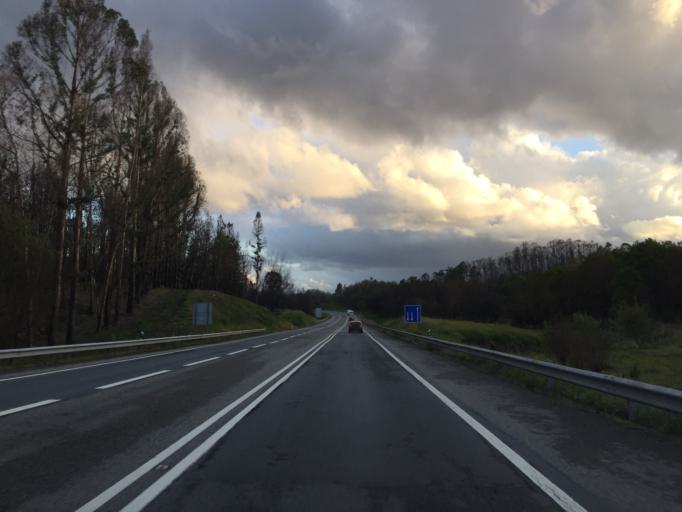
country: PT
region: Viseu
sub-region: Santa Comba Dao
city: Santa Comba Dao
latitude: 40.4253
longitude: -8.1179
